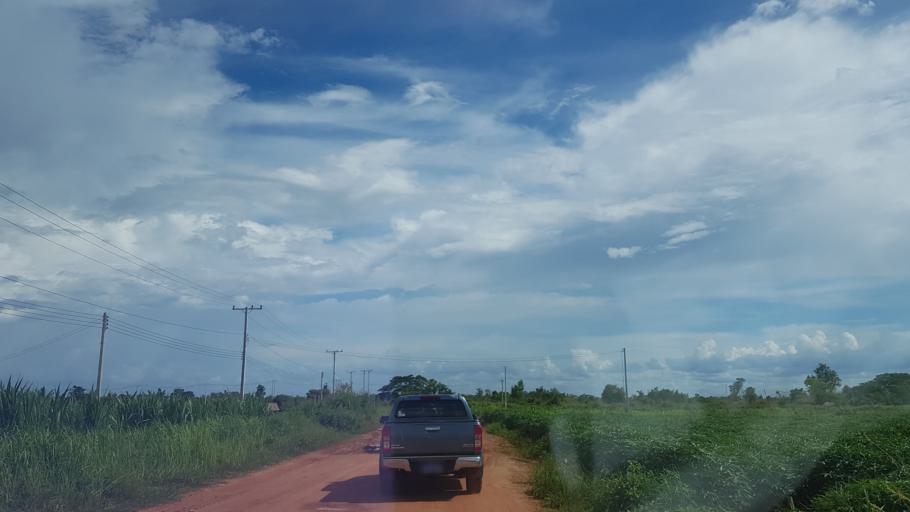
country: LA
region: Vientiane
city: Vientiane
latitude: 18.2114
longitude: 102.5660
